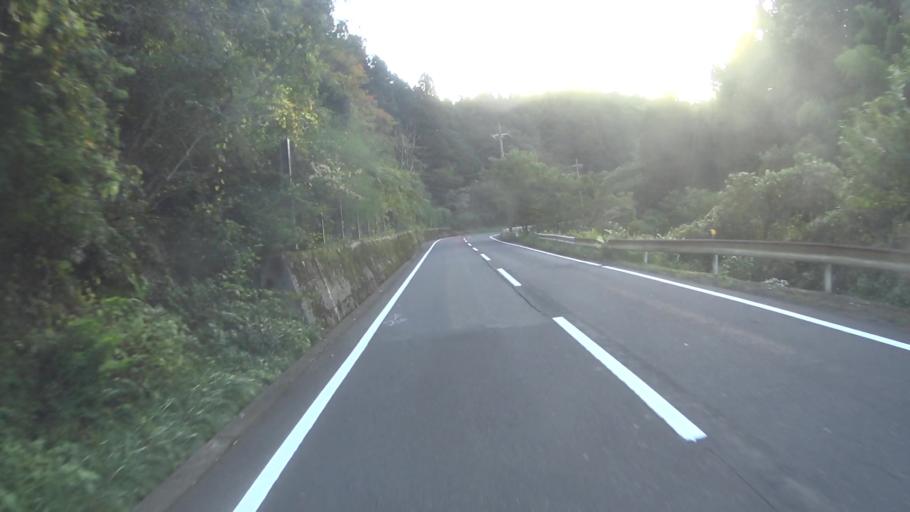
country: JP
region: Kyoto
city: Maizuru
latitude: 35.4620
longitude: 135.2573
